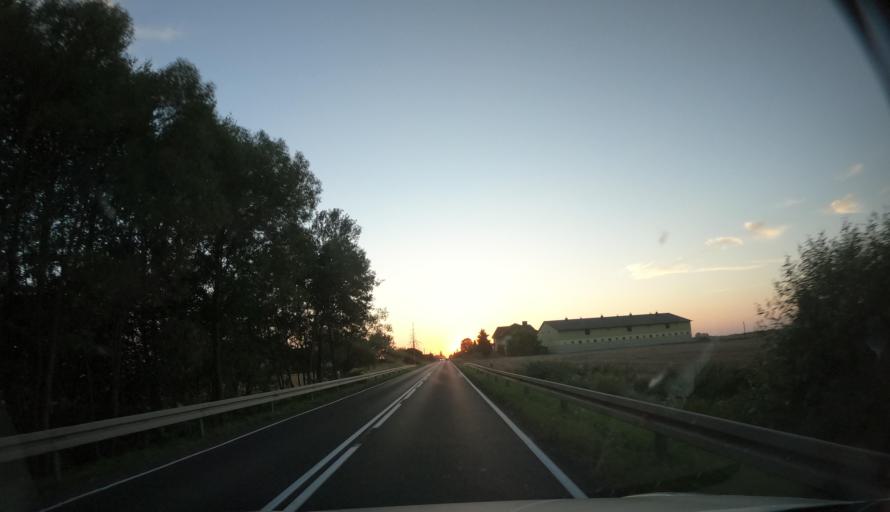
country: PL
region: Kujawsko-Pomorskie
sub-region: Powiat bydgoski
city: Koronowo
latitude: 53.3389
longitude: 17.8814
